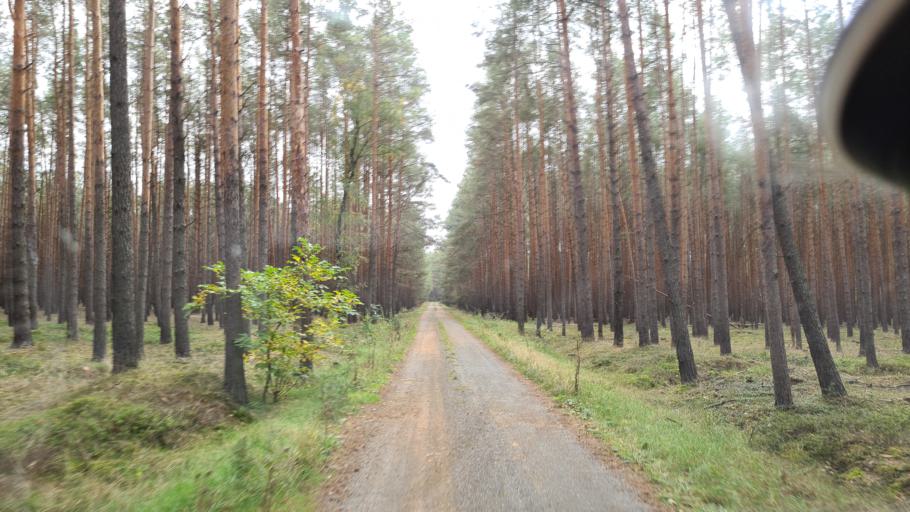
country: DE
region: Brandenburg
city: Schonewalde
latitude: 51.7119
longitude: 13.5772
